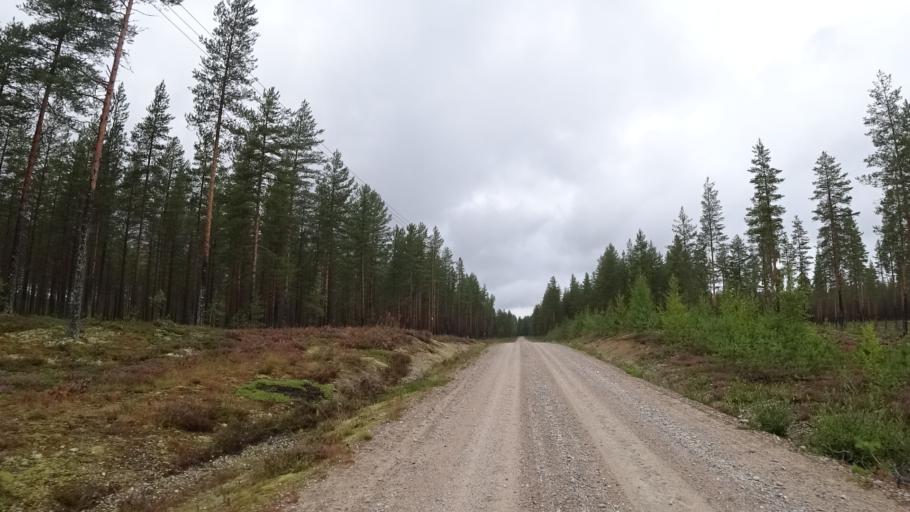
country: FI
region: North Karelia
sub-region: Pielisen Karjala
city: Lieksa
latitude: 63.5361
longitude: 30.0492
